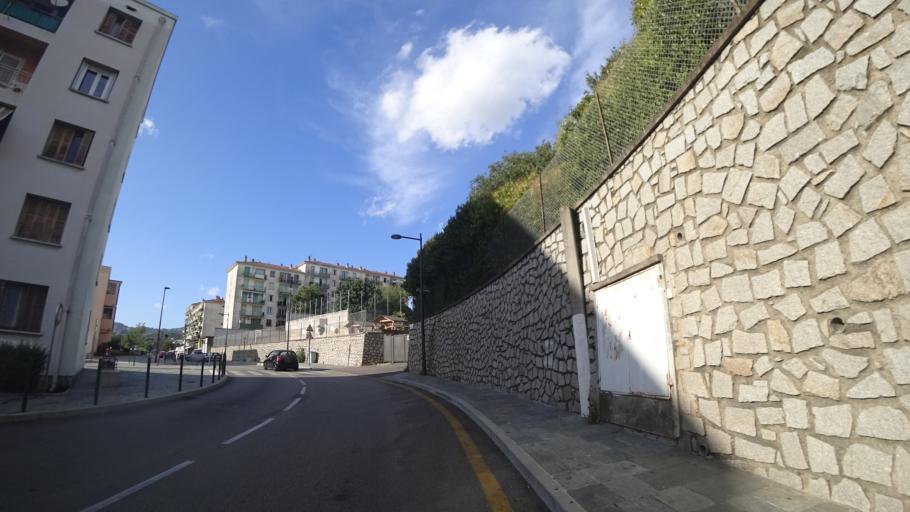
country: FR
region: Corsica
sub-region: Departement de la Corse-du-Sud
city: Ajaccio
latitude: 41.9347
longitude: 8.7436
